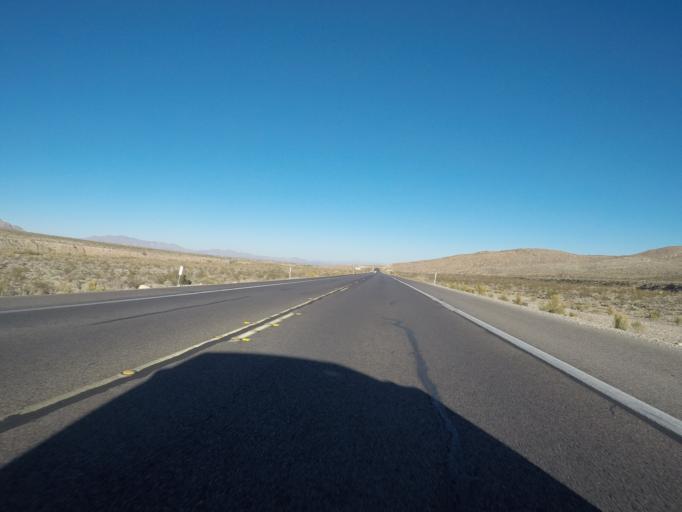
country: US
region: Nevada
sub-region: Clark County
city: Summerlin South
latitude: 36.1457
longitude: -115.3852
